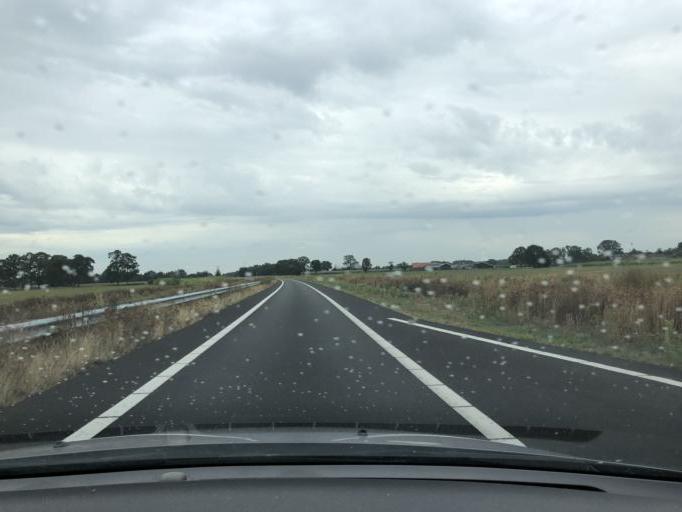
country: NL
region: Overijssel
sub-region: Gemeente Haaksbergen
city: Haaksbergen
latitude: 52.1551
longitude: 6.6877
